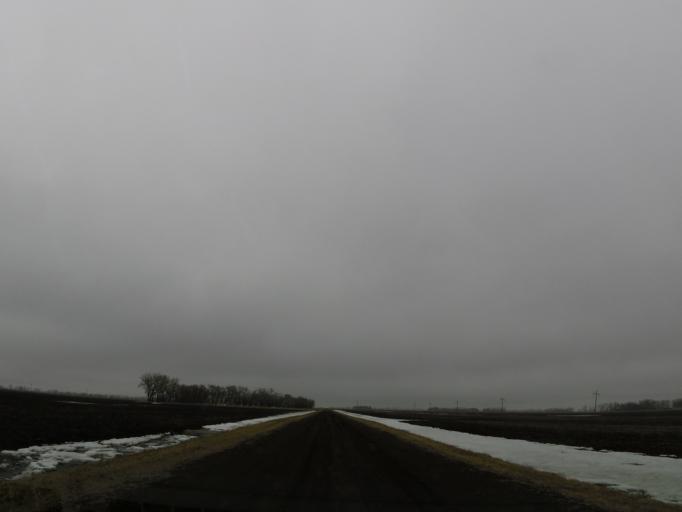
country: US
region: North Dakota
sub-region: Walsh County
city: Grafton
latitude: 48.4053
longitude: -97.2338
